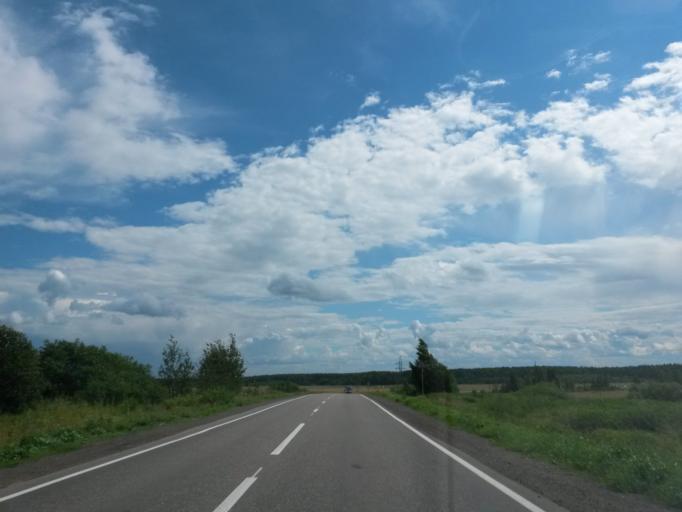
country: RU
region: Jaroslavl
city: Gavrilov-Yam
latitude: 57.3049
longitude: 39.9434
